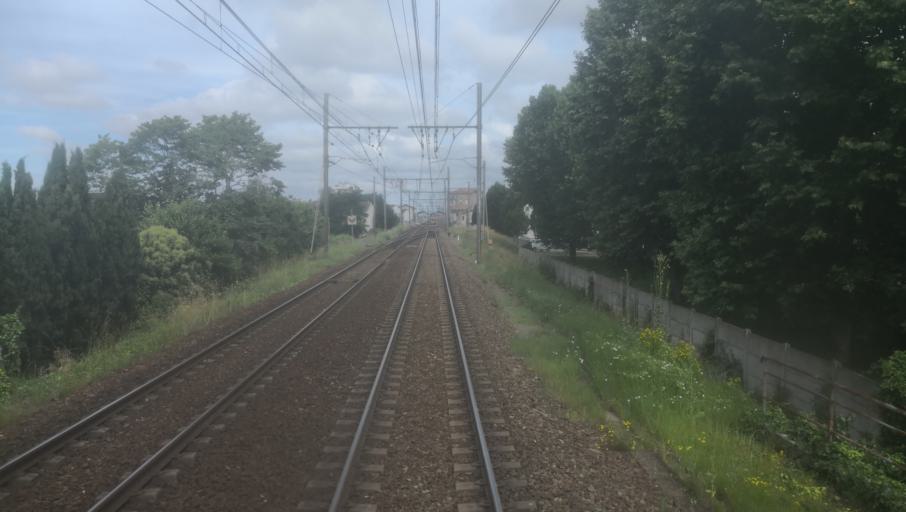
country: FR
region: Aquitaine
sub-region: Departement du Lot-et-Garonne
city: Marmande
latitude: 44.4999
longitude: 0.1737
